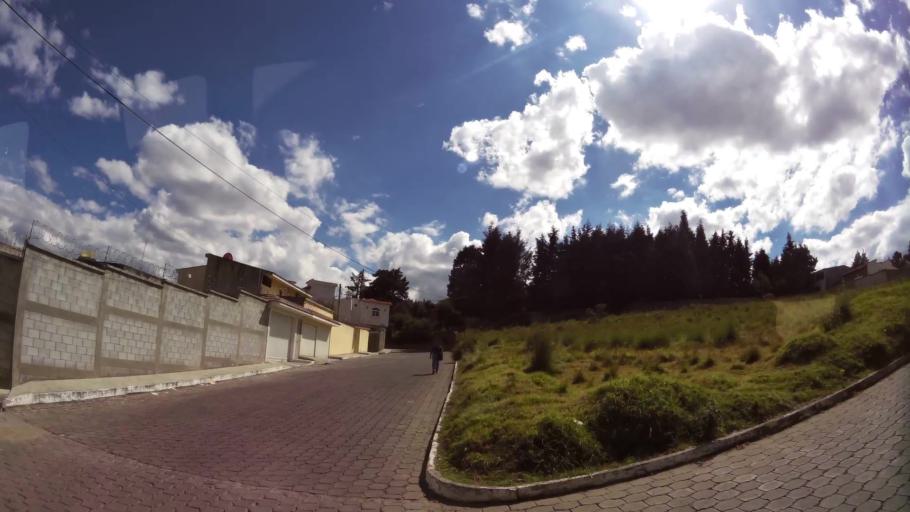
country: GT
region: Quetzaltenango
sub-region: Municipio de La Esperanza
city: La Esperanza
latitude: 14.8491
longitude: -91.5438
